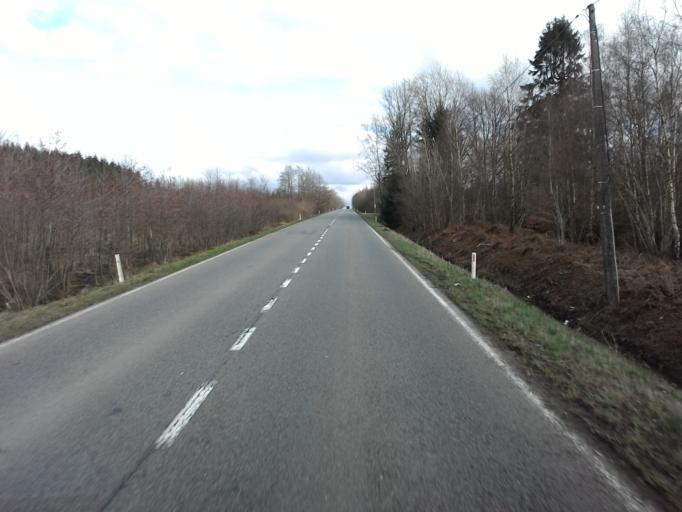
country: BE
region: Wallonia
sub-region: Province de Liege
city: Ferrieres
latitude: 50.3845
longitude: 5.6652
